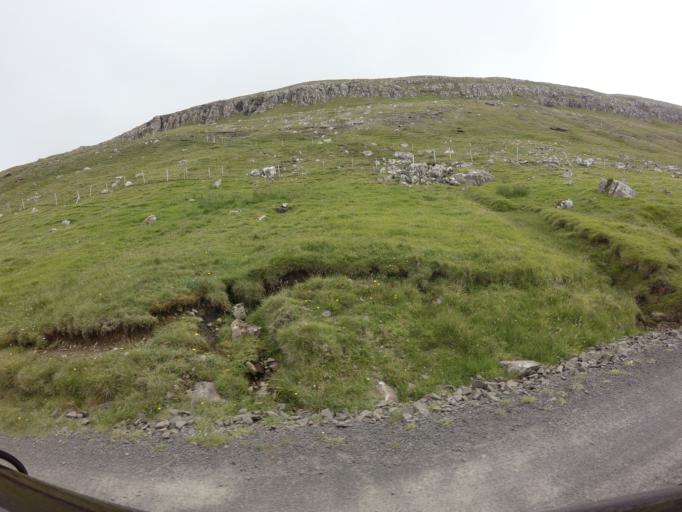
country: FO
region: Sandoy
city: Sandur
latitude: 61.8068
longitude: -6.7529
